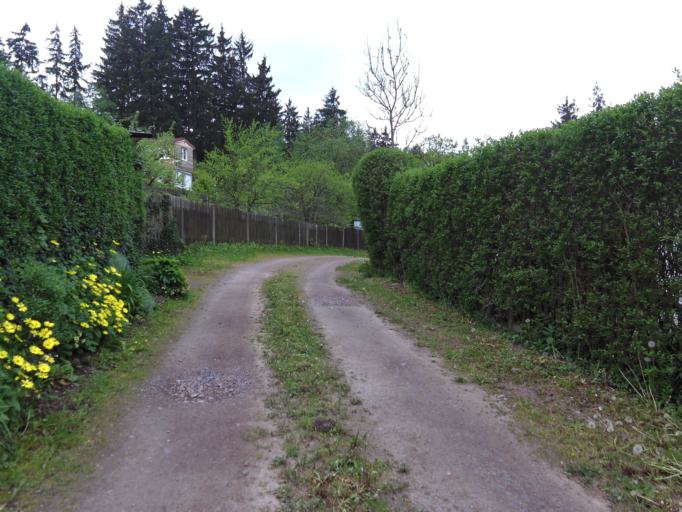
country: DE
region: Thuringia
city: Georgenthal
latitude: 50.8257
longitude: 10.6595
